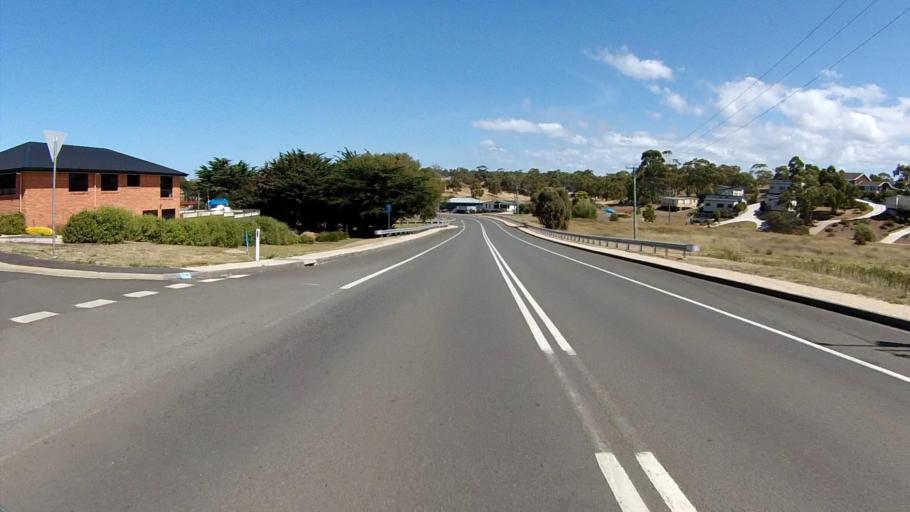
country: AU
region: Tasmania
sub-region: Break O'Day
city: St Helens
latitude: -42.1288
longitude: 148.0735
